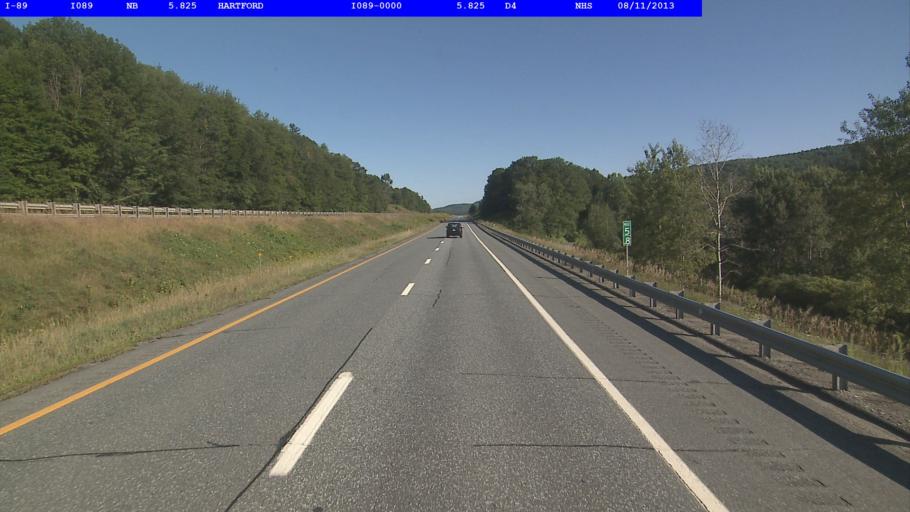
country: US
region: Vermont
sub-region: Windsor County
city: White River Junction
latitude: 43.6897
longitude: -72.4045
